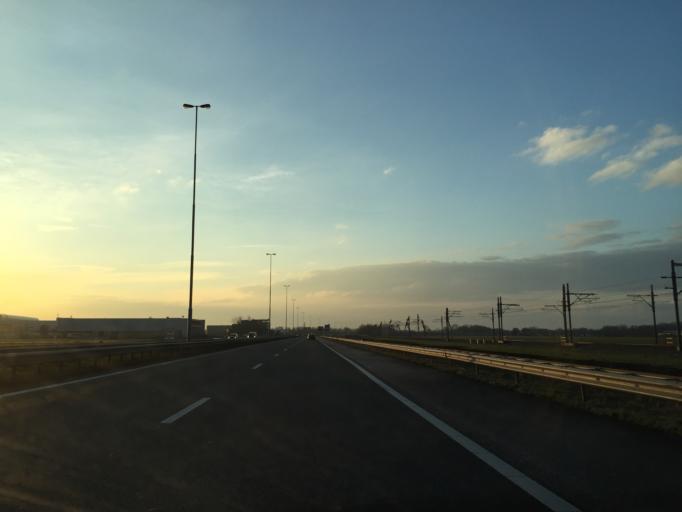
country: NL
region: North Brabant
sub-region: Gemeente Woudrichem
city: Woudrichem
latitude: 51.8417
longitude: 5.0200
